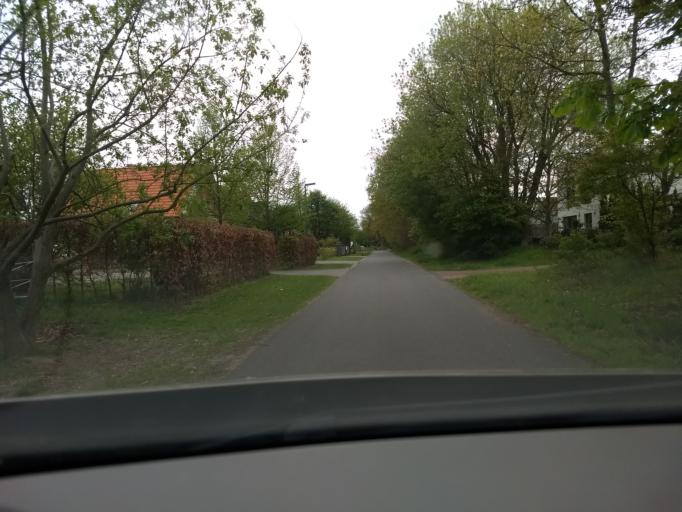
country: DE
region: Lower Saxony
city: Rastede
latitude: 53.2321
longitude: 8.2143
